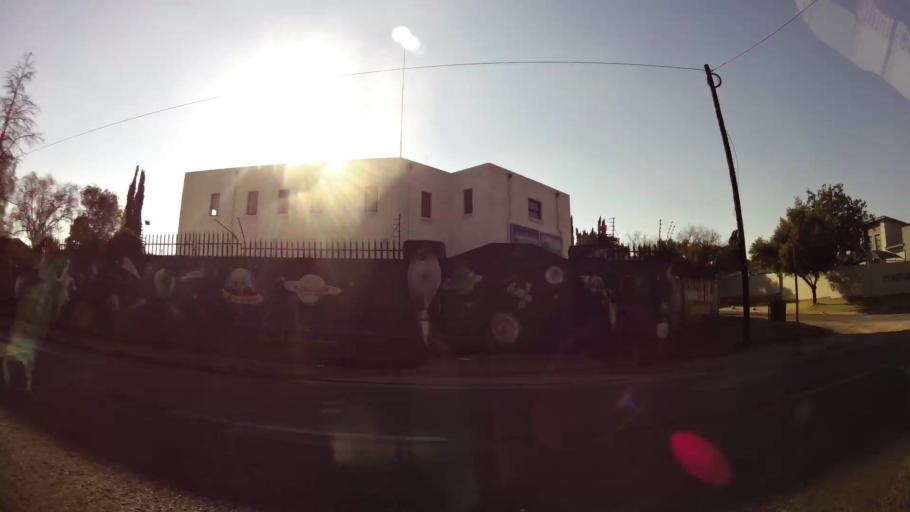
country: ZA
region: Gauteng
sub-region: City of Johannesburg Metropolitan Municipality
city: Modderfontein
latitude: -26.1412
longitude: 28.1658
